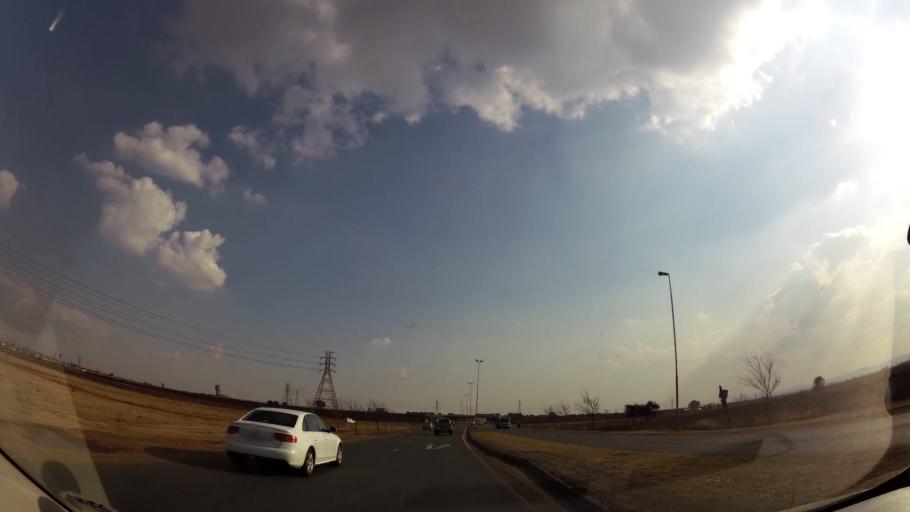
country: ZA
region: Gauteng
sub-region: Ekurhuleni Metropolitan Municipality
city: Germiston
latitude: -26.3398
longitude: 28.2240
